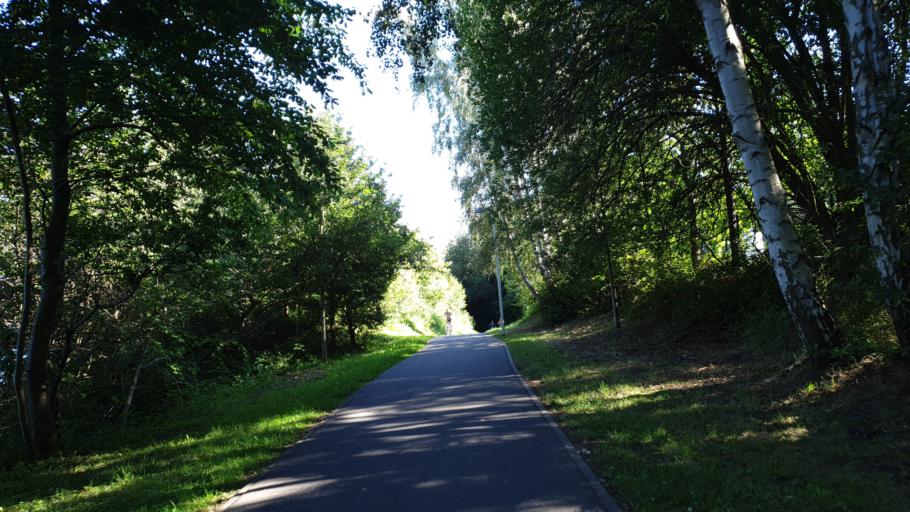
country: DE
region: Mecklenburg-Vorpommern
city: Kramerhof
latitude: 54.3395
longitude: 13.0771
